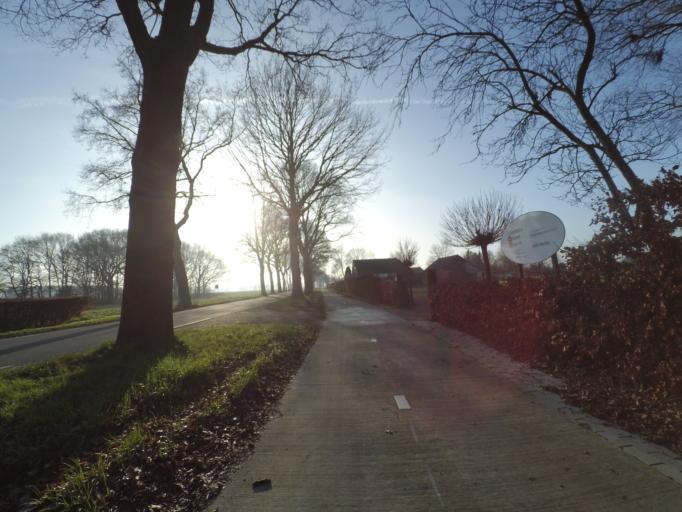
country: NL
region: Drenthe
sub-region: Gemeente Assen
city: Assen
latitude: 52.8756
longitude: 6.6427
